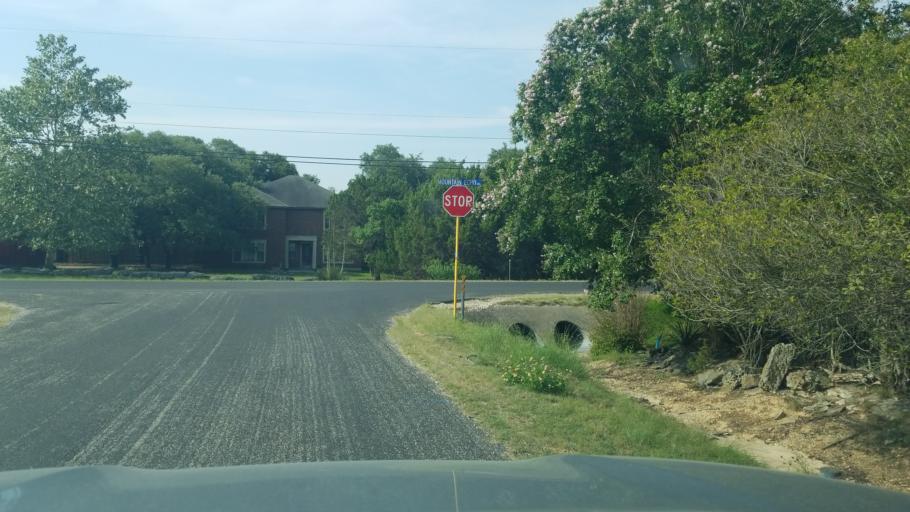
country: US
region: Texas
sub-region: Bexar County
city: Timberwood Park
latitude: 29.7000
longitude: -98.4954
